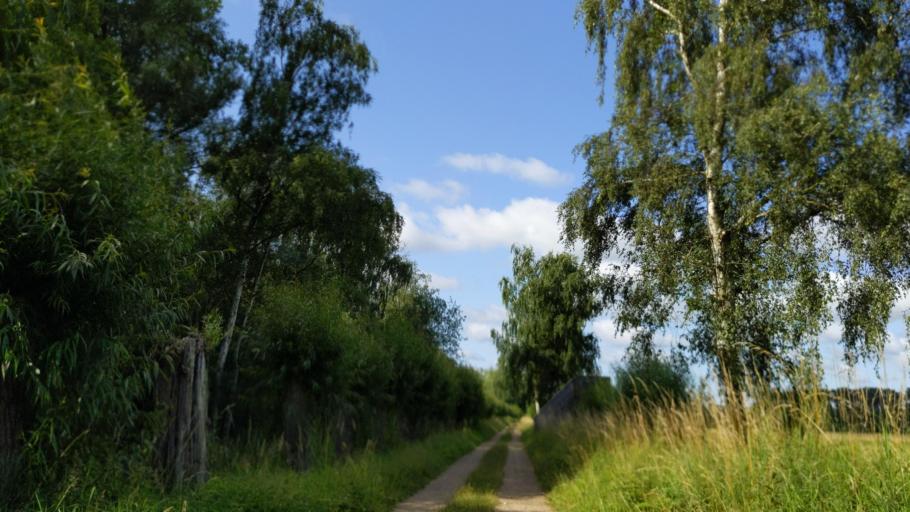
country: DE
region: Schleswig-Holstein
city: Travemuende
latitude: 53.9468
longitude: 10.8759
